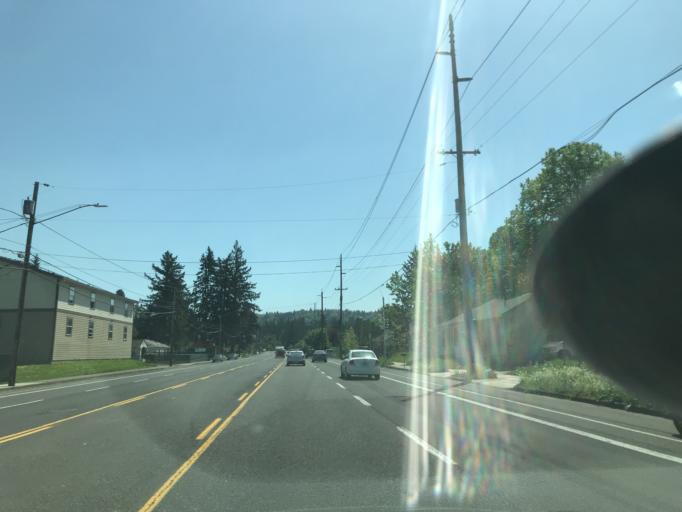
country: US
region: Oregon
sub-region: Multnomah County
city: Lents
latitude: 45.4855
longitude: -122.5379
